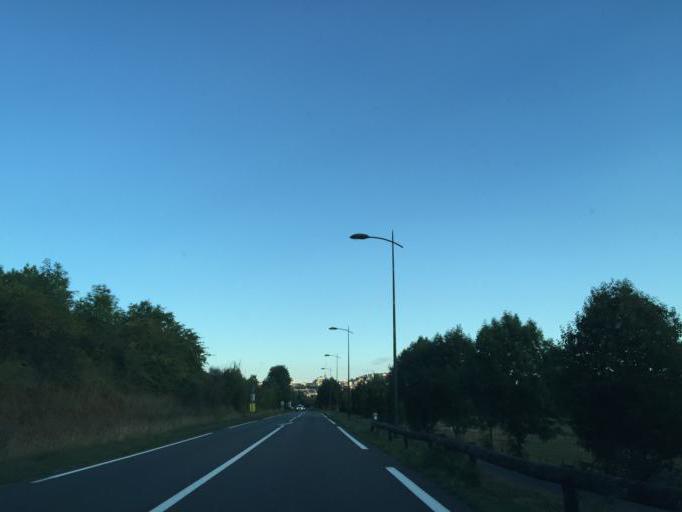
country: FR
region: Midi-Pyrenees
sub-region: Departement de l'Aveyron
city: Rodez
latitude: 44.3753
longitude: 2.5656
